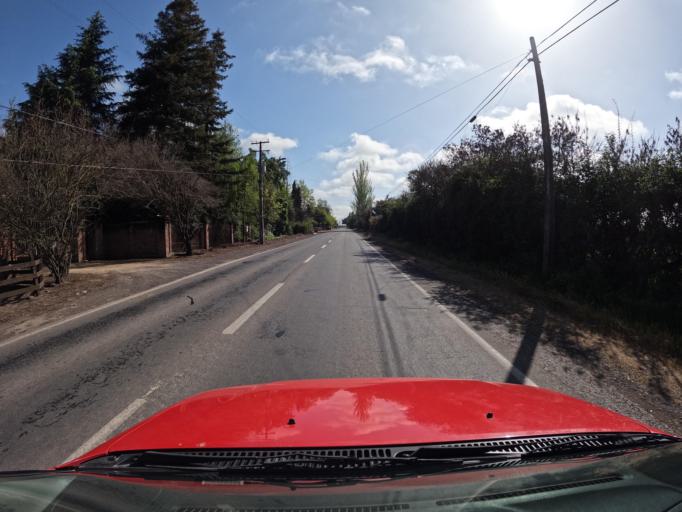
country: CL
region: Maule
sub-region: Provincia de Curico
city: Rauco
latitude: -34.9053
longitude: -71.2782
